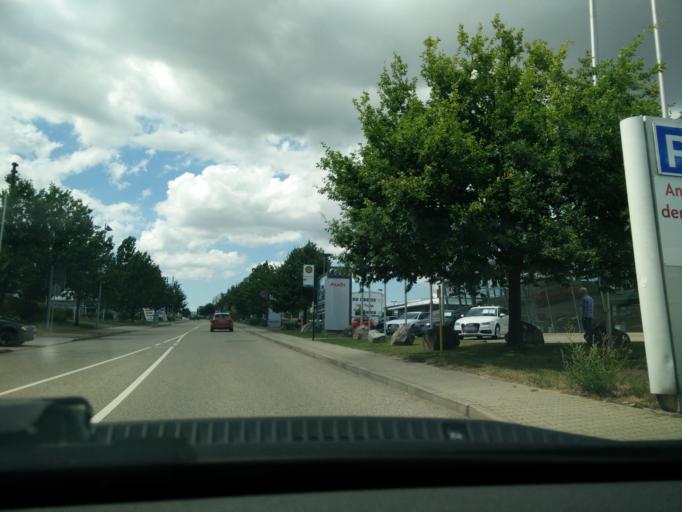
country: DE
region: Saxony
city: Wittgensdorf
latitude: 50.8669
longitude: 12.8579
